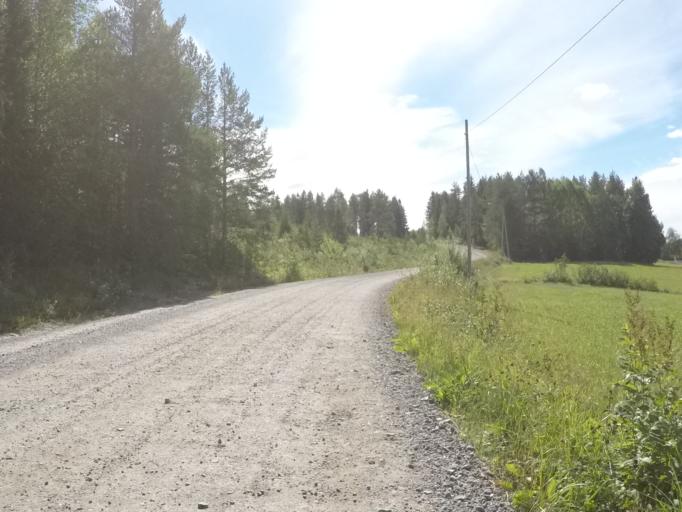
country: SE
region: Vaesterbotten
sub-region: Robertsfors Kommun
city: Robertsfors
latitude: 64.0042
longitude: 20.8129
